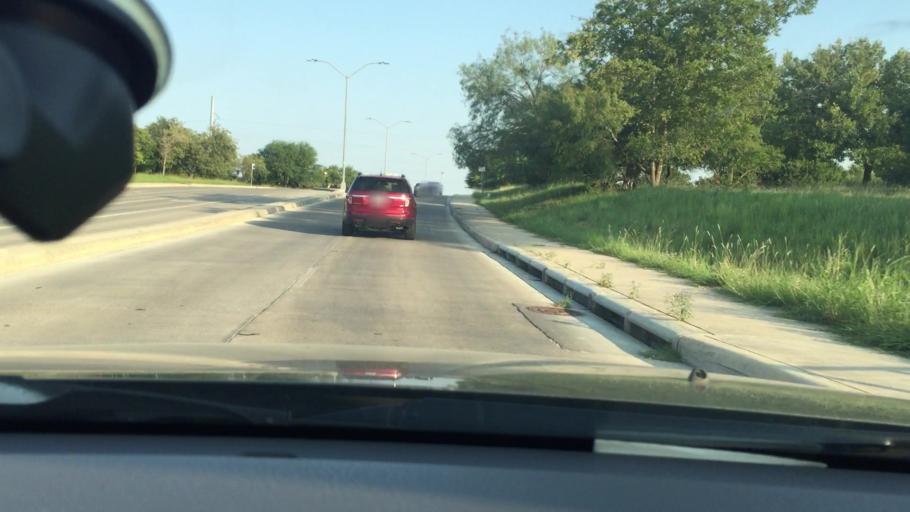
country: US
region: Texas
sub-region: Bexar County
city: Leon Valley
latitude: 29.5199
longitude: -98.5883
